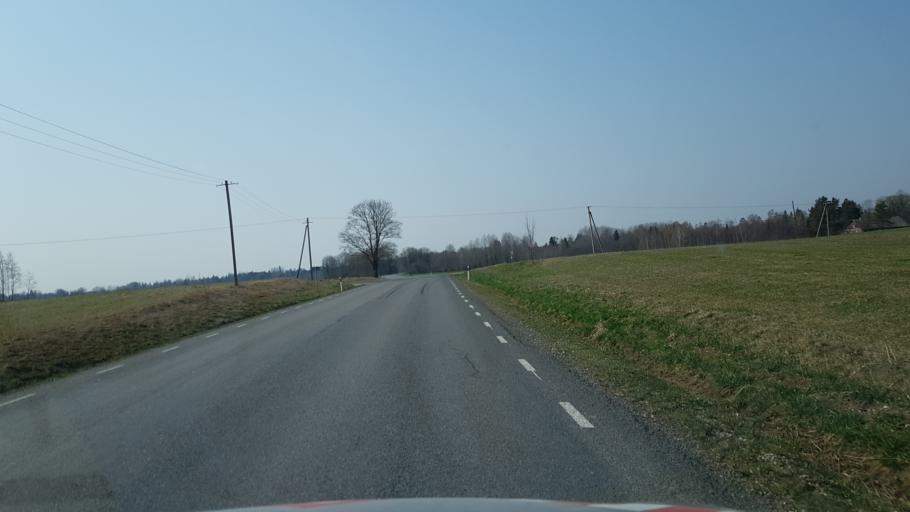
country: EE
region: Raplamaa
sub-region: Kehtna vald
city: Kehtna
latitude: 59.0405
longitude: 24.9382
